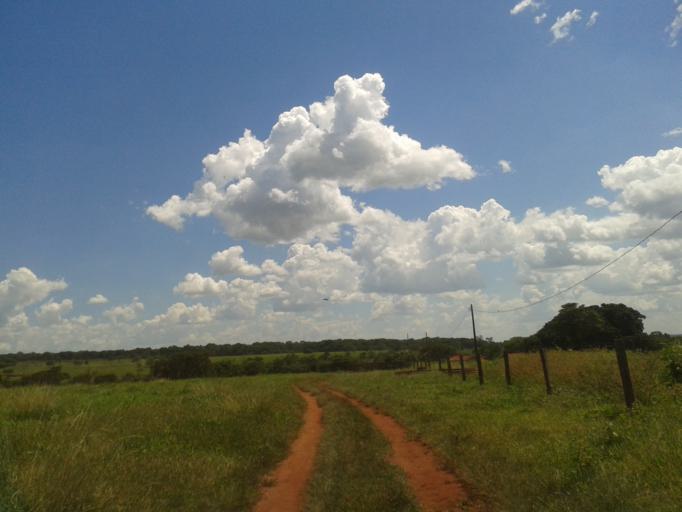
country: BR
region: Minas Gerais
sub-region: Santa Vitoria
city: Santa Vitoria
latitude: -19.1069
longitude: -50.5215
